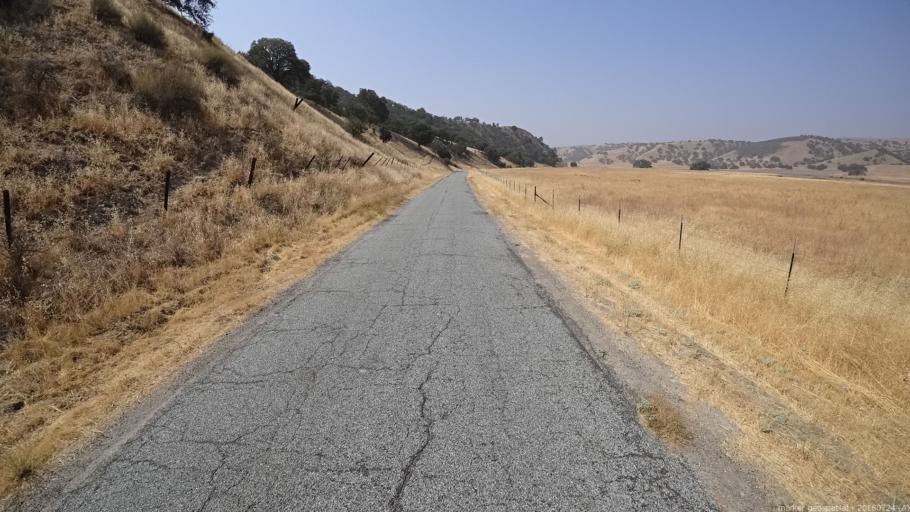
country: US
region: California
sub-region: San Luis Obispo County
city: San Miguel
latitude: 35.9059
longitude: -120.6925
